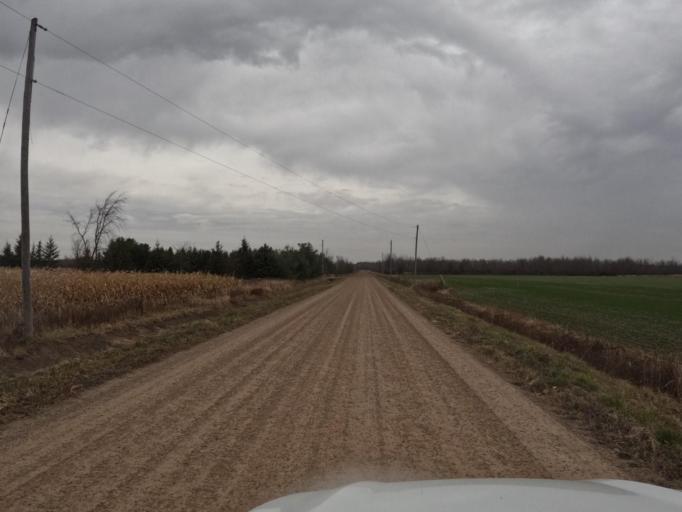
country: CA
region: Ontario
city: Shelburne
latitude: 43.8906
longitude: -80.3832
